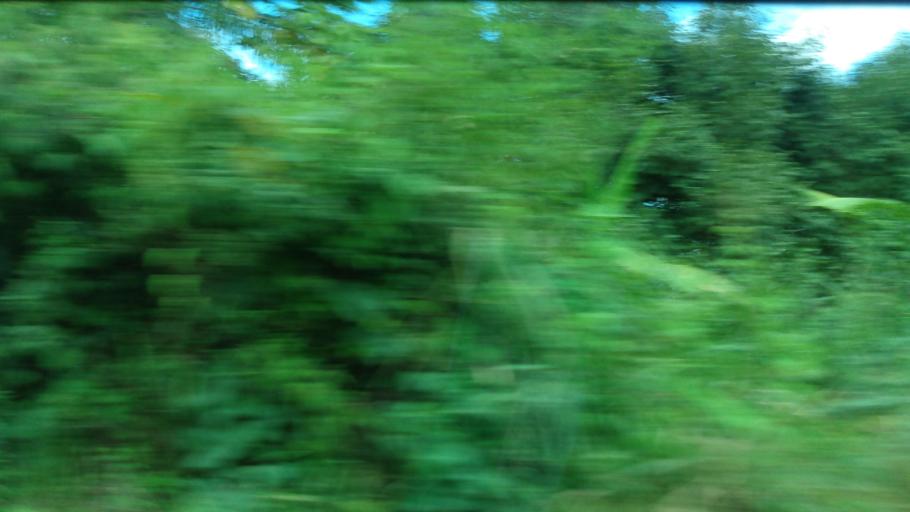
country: BR
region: Pernambuco
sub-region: Catende
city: Catende
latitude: -8.6930
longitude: -35.7245
